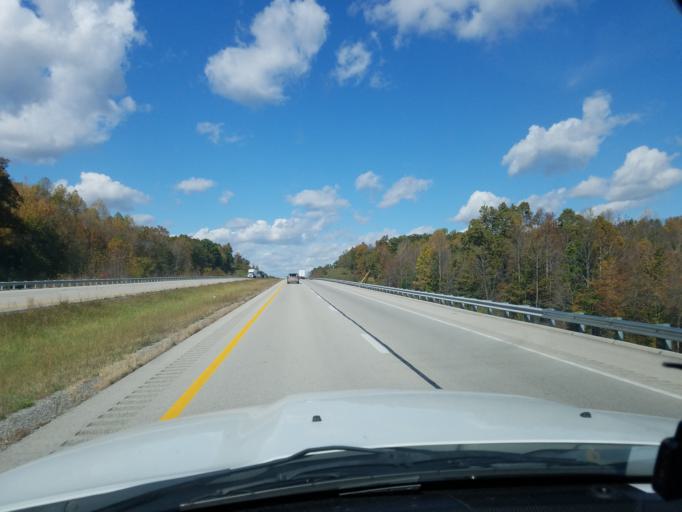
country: US
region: Kentucky
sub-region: Ohio County
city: Hartford
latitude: 37.5643
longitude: -86.9456
